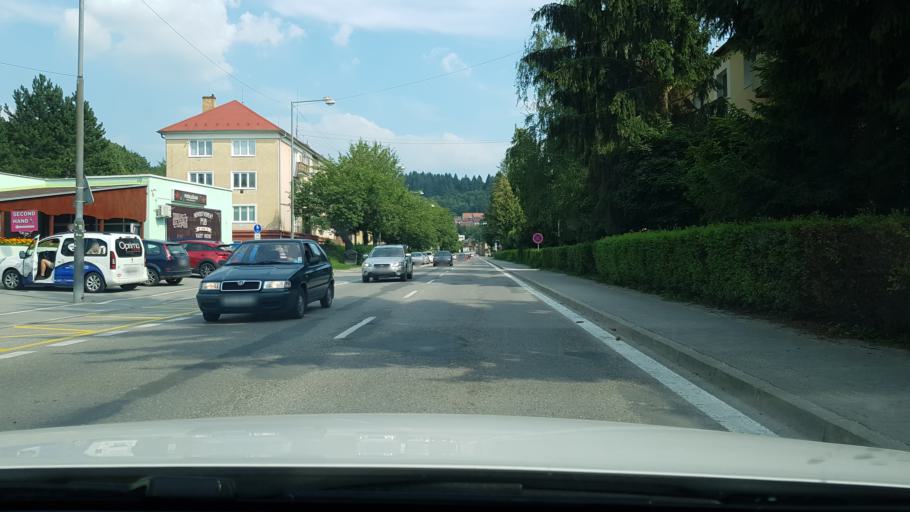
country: SK
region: Trenciansky
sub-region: Okres Povazska Bystrica
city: Povazska Bystrica
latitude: 49.1091
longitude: 18.4565
